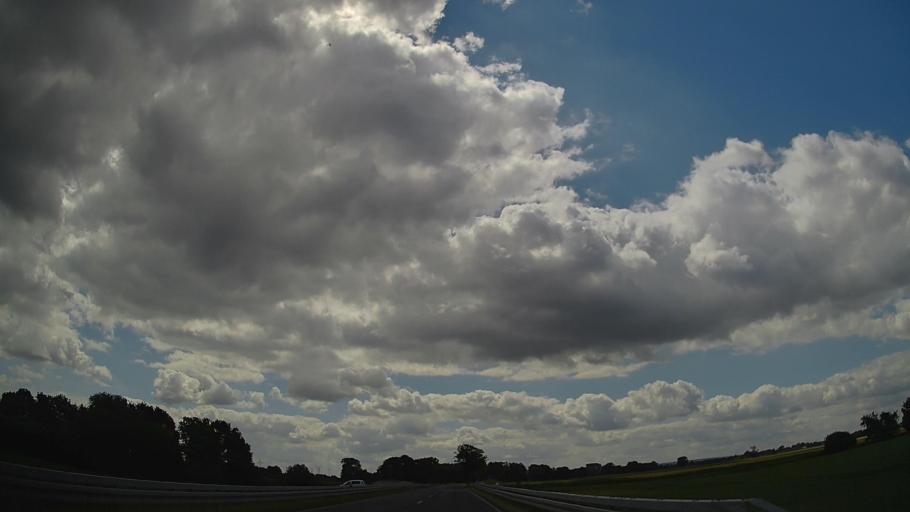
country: DE
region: Lower Saxony
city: Lembruch
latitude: 52.5471
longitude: 8.3717
